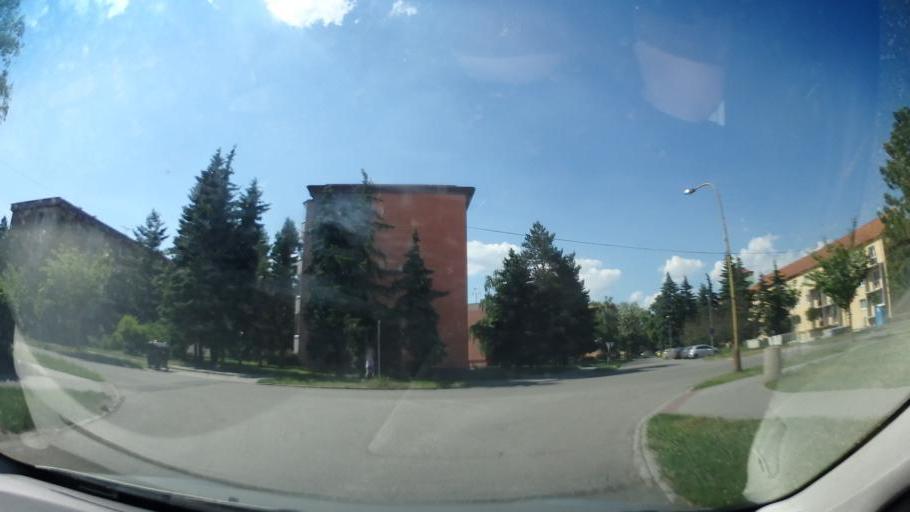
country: CZ
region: Zlin
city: Chropyne
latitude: 49.3617
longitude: 17.3630
